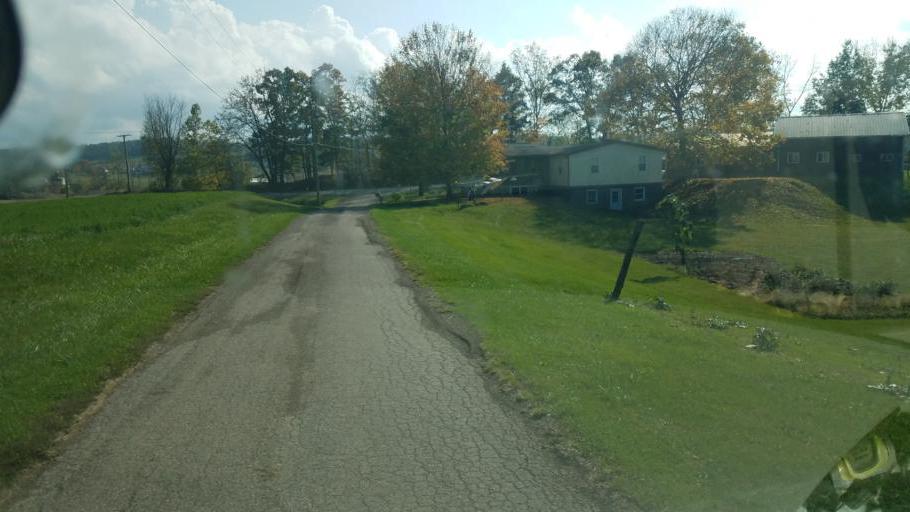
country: US
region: Ohio
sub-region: Holmes County
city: Millersburg
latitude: 40.6205
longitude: -81.8775
